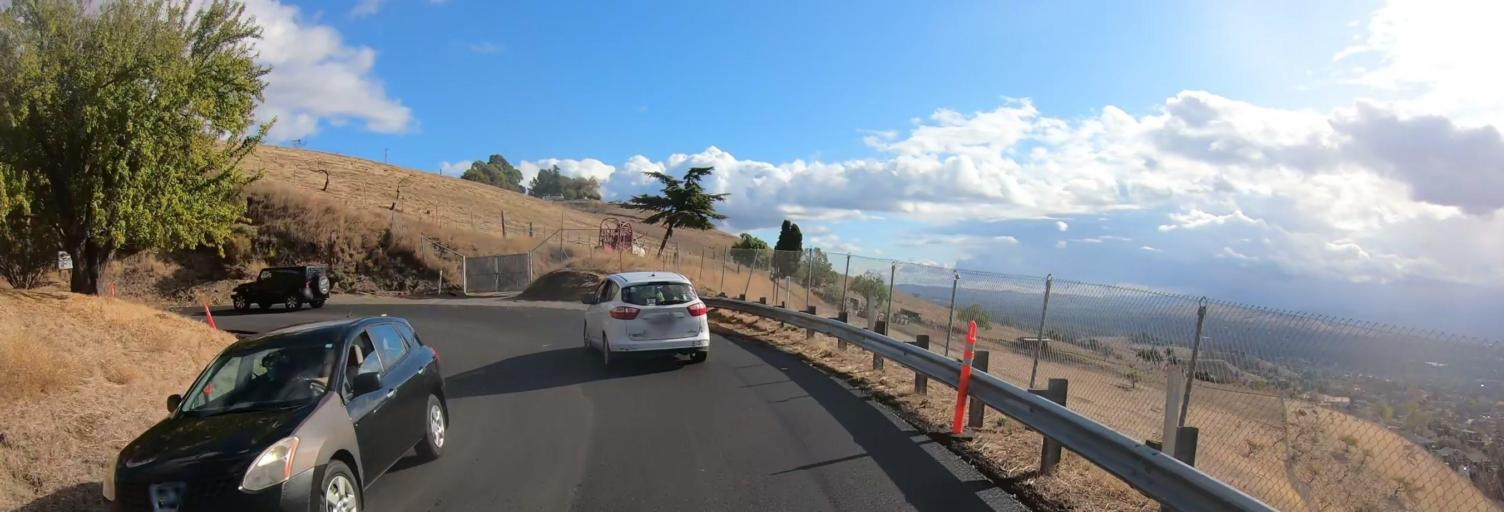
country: US
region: California
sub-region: Santa Clara County
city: East Foothills
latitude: 37.3743
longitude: -121.7986
